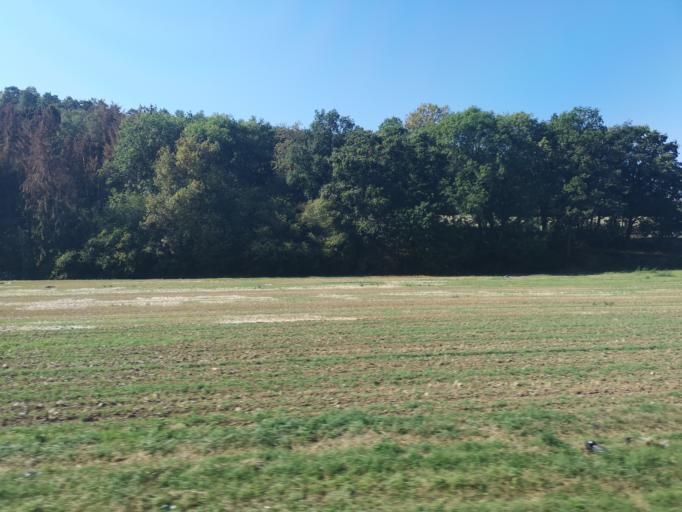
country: DE
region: North Rhine-Westphalia
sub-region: Regierungsbezirk Koln
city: Kreuzau
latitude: 50.7262
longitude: 6.4668
